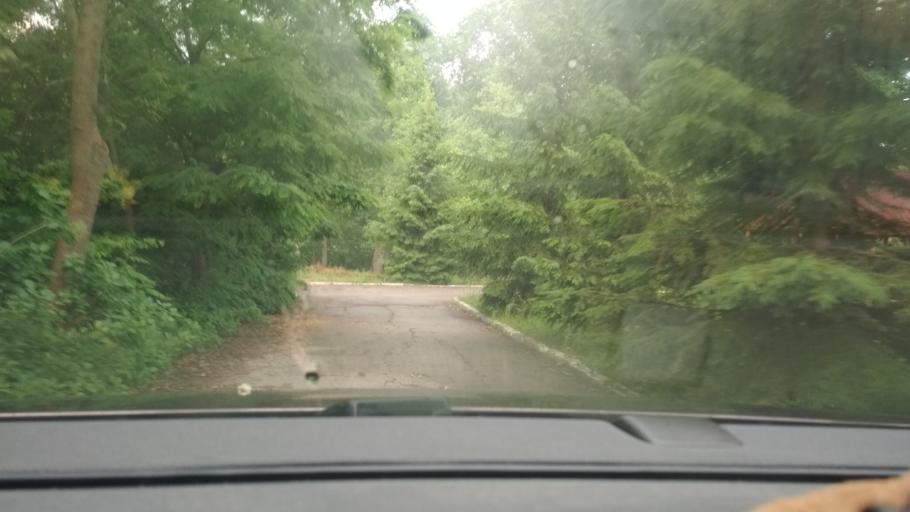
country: MD
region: Singerei
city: Biruinta
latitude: 47.7503
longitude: 28.1386
